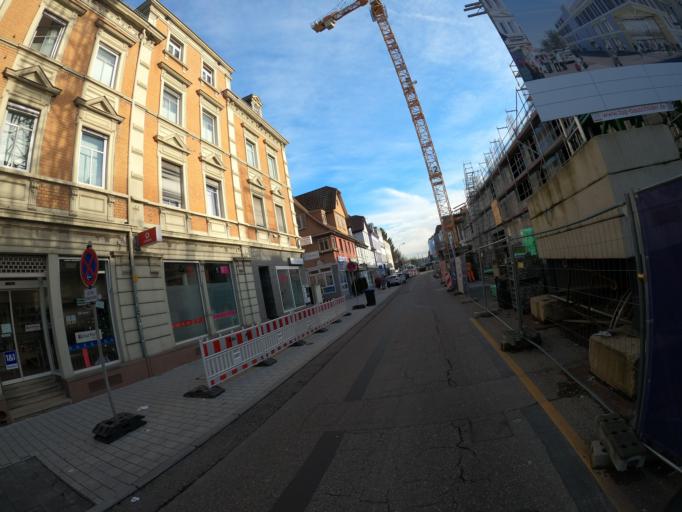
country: DE
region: Baden-Wuerttemberg
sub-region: Regierungsbezirk Stuttgart
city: Goeppingen
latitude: 48.7025
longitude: 9.6576
